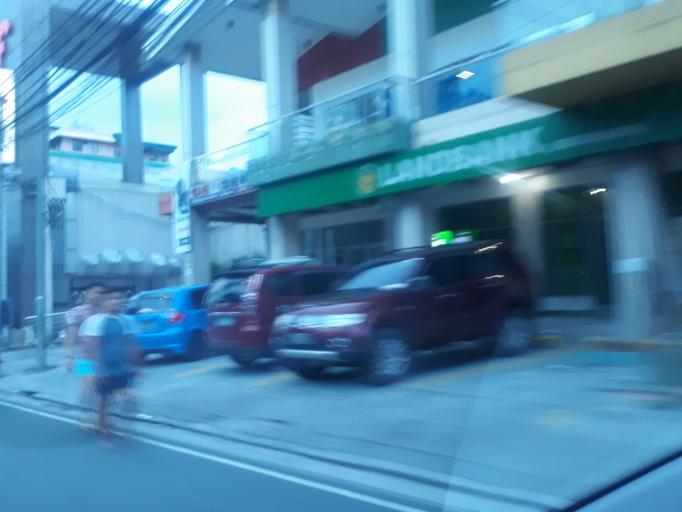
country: PH
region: Calabarzon
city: Del Monte
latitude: 14.6237
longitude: 121.0084
